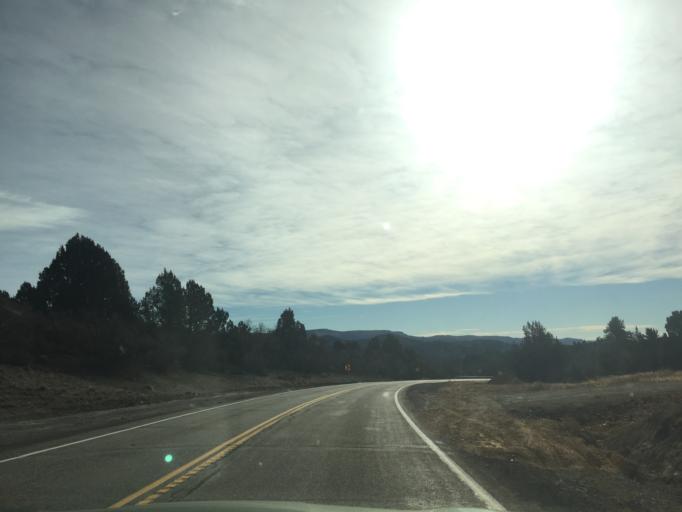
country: US
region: Utah
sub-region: Garfield County
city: Panguitch
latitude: 37.4964
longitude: -112.5320
